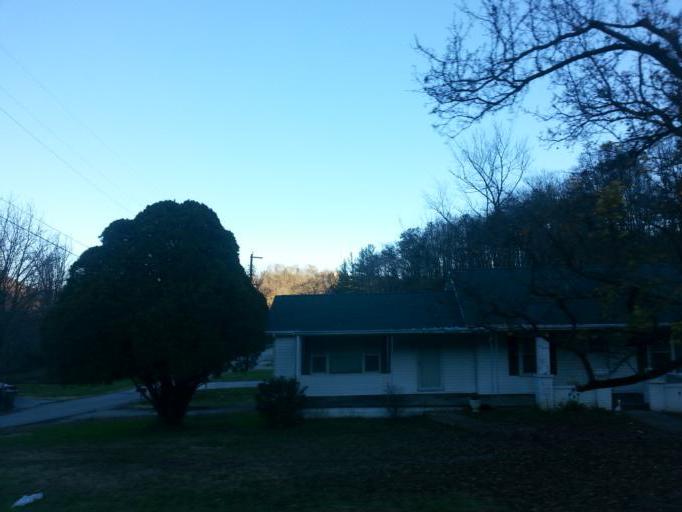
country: US
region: Tennessee
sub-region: Anderson County
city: Rocky Top
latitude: 36.2152
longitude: -84.1528
